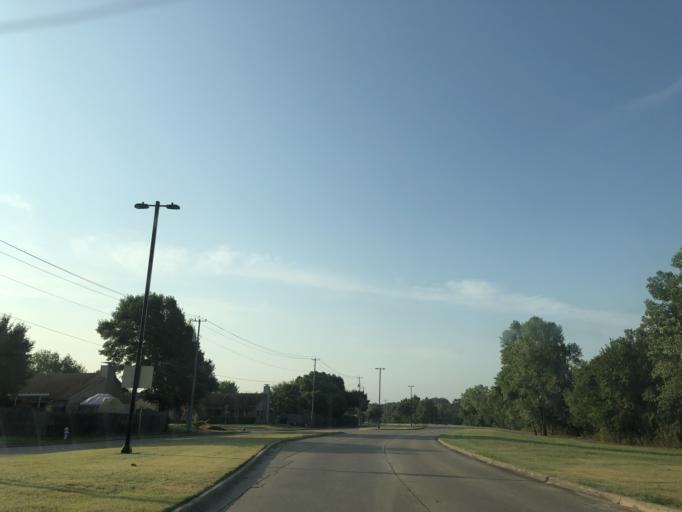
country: US
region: Texas
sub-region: Dallas County
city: Garland
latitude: 32.8692
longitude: -96.6284
